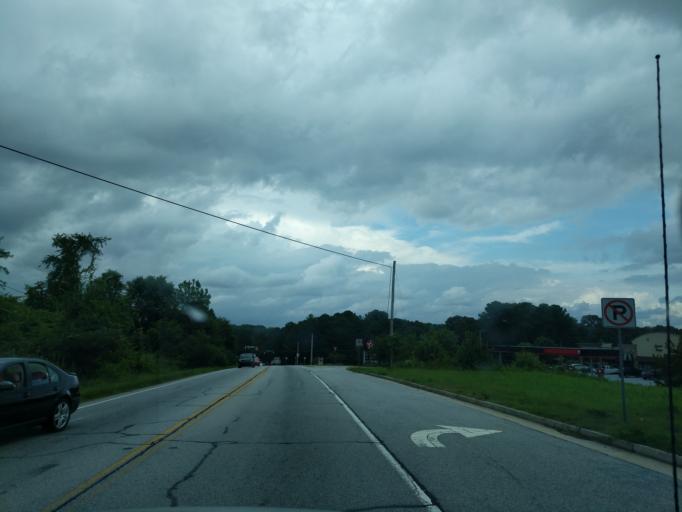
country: US
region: Georgia
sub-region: Walton County
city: Loganville
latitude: 33.8296
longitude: -83.9150
